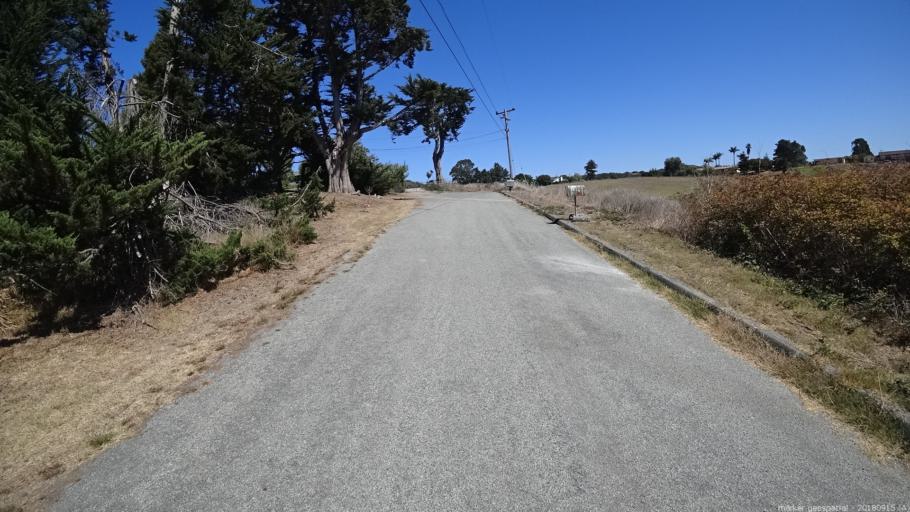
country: US
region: California
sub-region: Monterey County
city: Las Lomas
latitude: 36.8715
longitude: -121.7518
